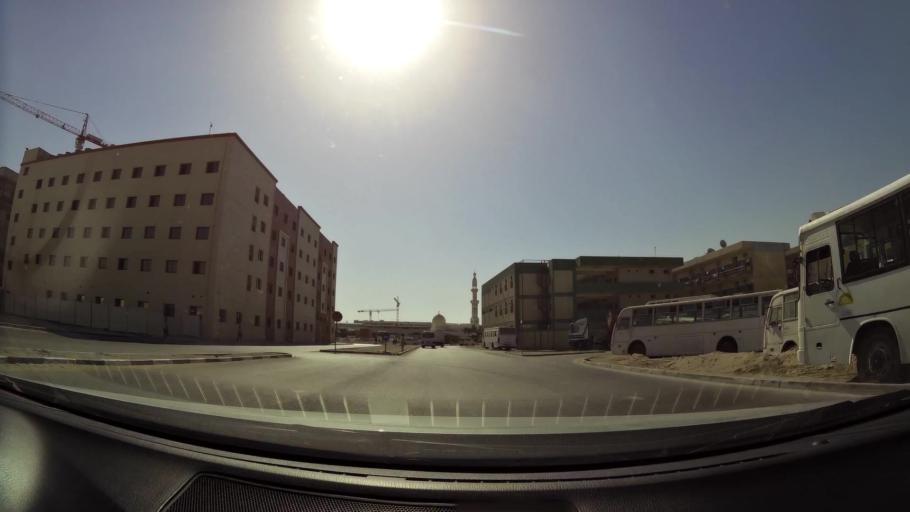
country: AE
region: Dubai
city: Dubai
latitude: 25.0056
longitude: 55.1083
